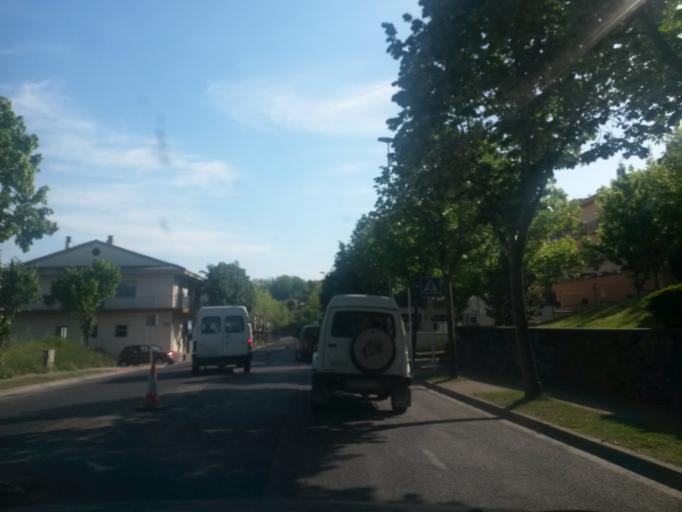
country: ES
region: Catalonia
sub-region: Provincia de Girona
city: Olot
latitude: 42.1814
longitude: 2.4971
